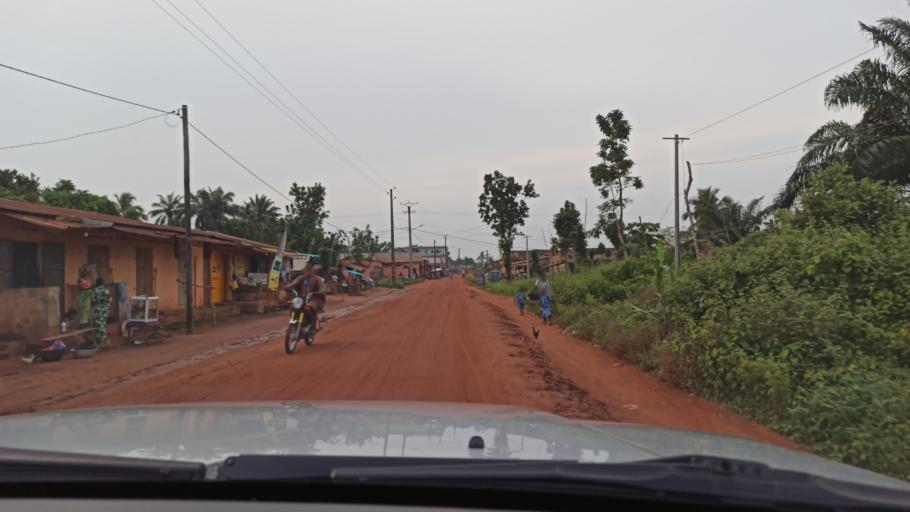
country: BJ
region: Queme
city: Porto-Novo
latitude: 6.5210
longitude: 2.6744
